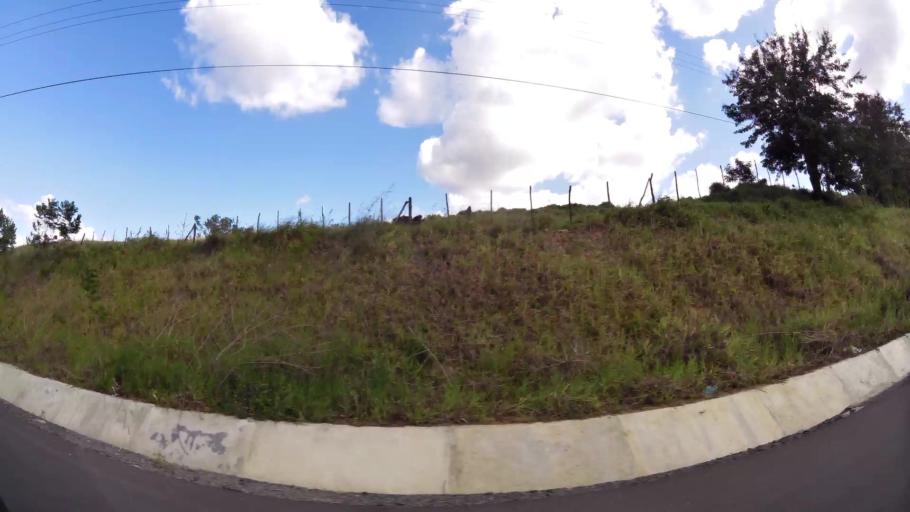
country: DO
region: Santo Domingo
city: Santo Domingo Oeste
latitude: 18.5499
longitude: -70.0769
